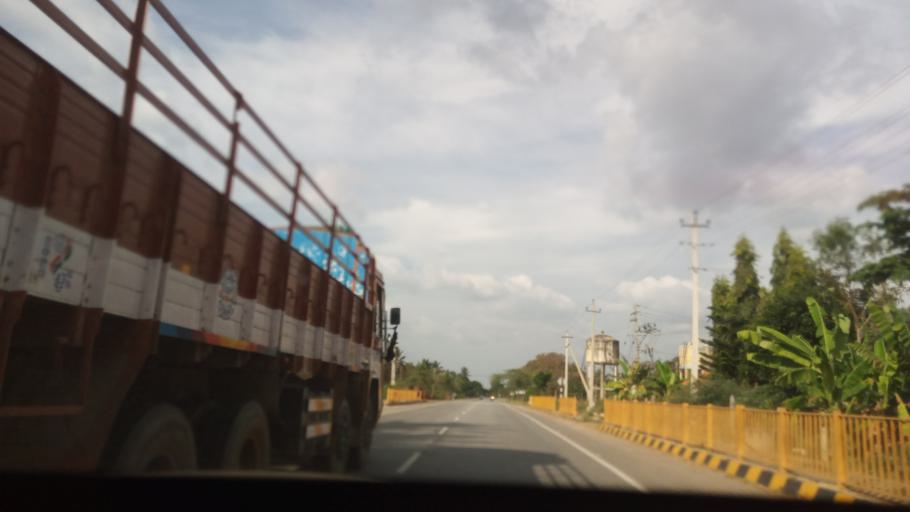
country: IN
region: Karnataka
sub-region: Mandya
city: Maddur
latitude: 12.6694
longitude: 77.0550
